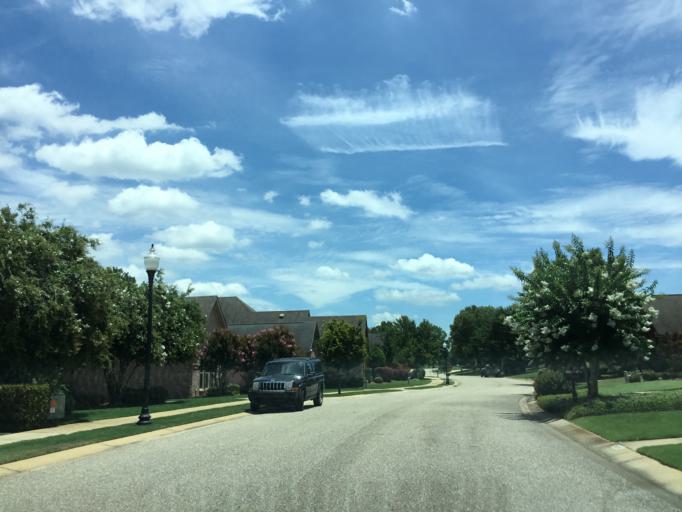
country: US
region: Alabama
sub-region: Montgomery County
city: Pike Road
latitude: 32.3726
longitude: -86.1395
